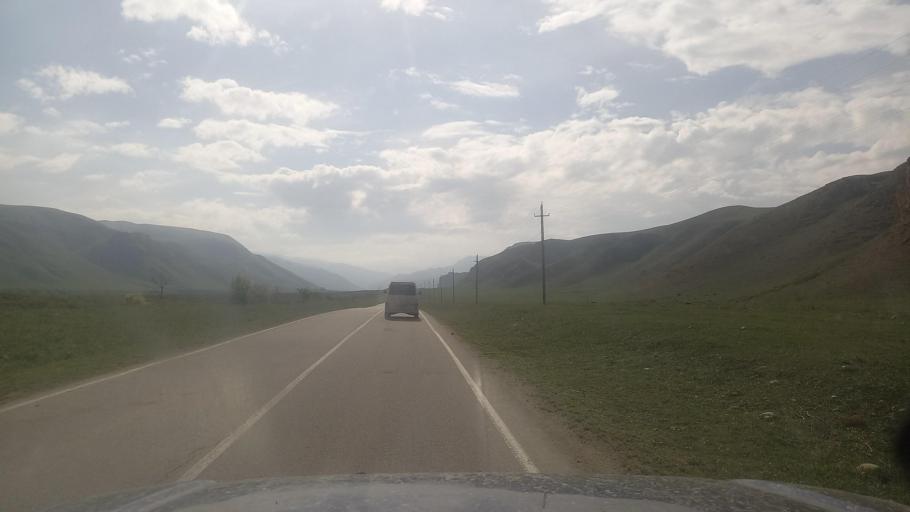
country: RU
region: Kabardino-Balkariya
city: Kamennomostskoye
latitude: 43.7359
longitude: 42.9893
